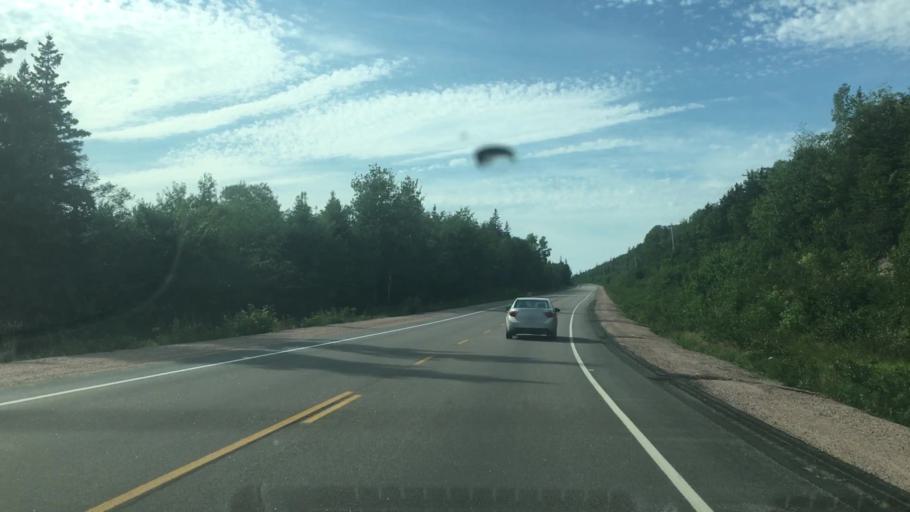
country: CA
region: Nova Scotia
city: Sydney Mines
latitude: 46.8152
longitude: -60.3413
